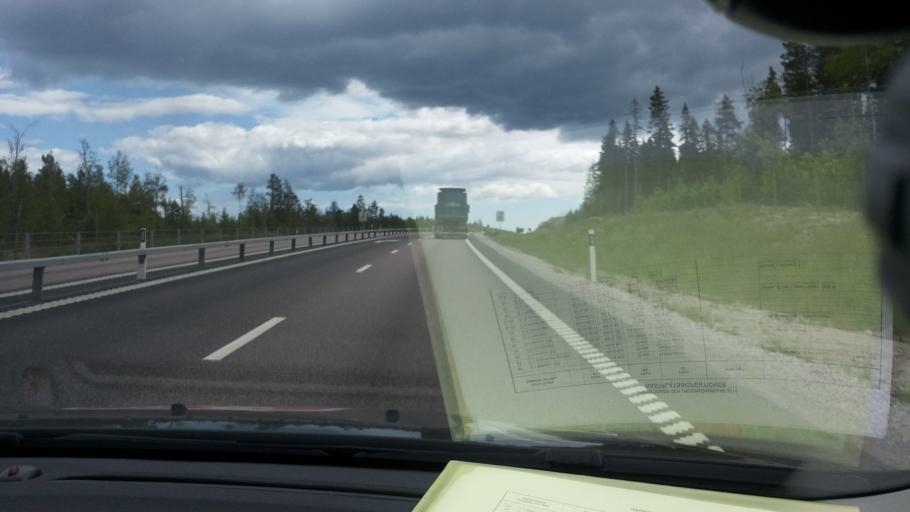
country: SE
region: Vaesternorrland
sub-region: Sundsvalls Kommun
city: Njurundabommen
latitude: 62.2623
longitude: 17.3597
